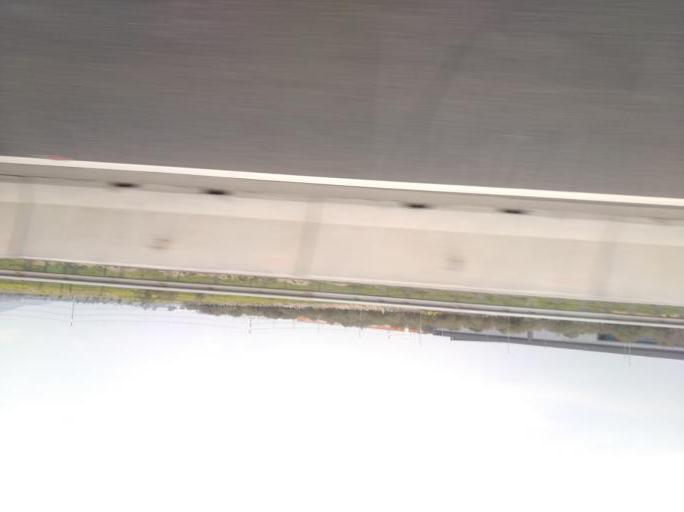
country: CL
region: Santiago Metropolitan
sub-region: Provincia de Santiago
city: Lo Prado
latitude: -33.4264
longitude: -70.8013
